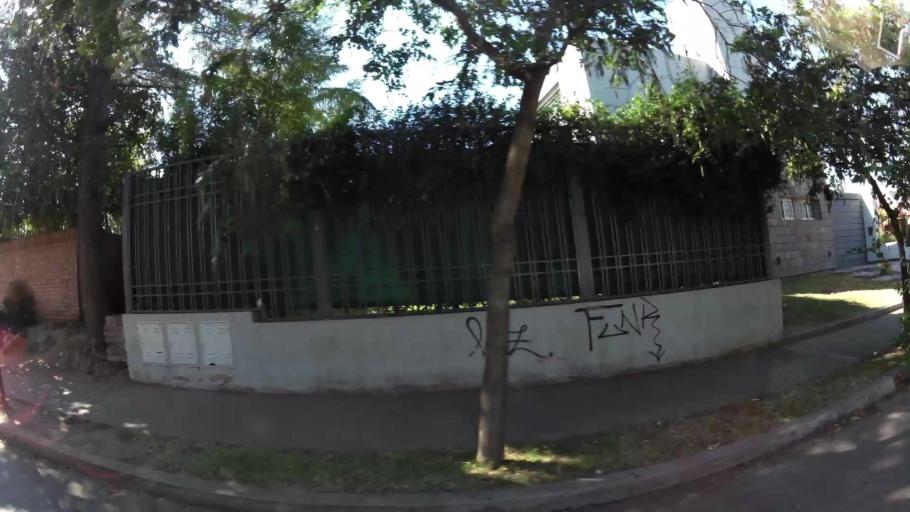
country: AR
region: Cordoba
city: Villa Allende
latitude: -31.3503
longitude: -64.2465
